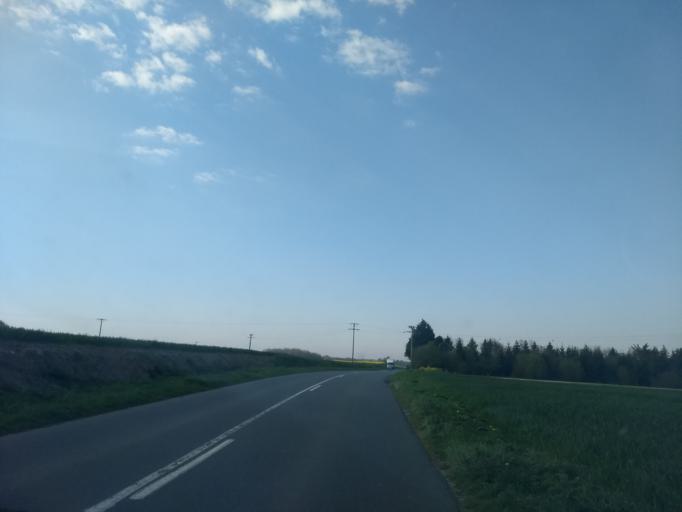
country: FR
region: Picardie
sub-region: Departement de la Somme
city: Poulainville
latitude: 49.9440
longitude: 2.3582
